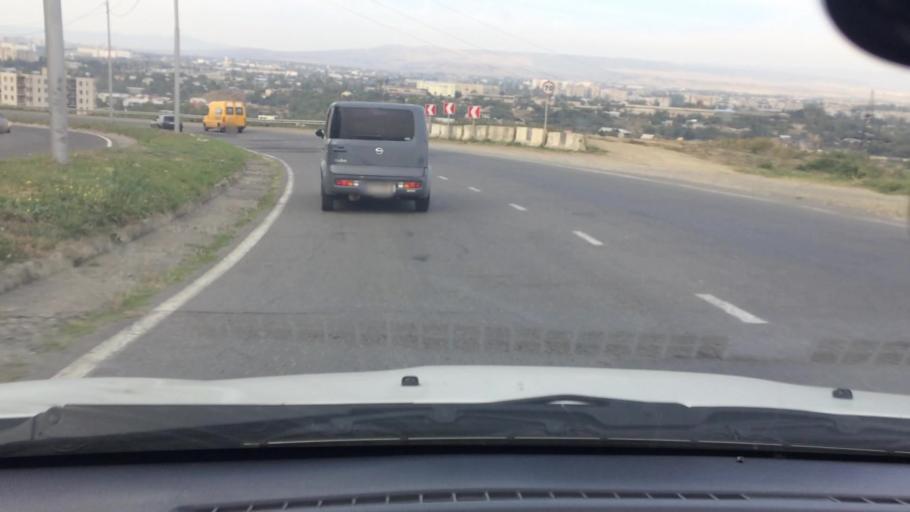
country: GE
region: T'bilisi
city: Tbilisi
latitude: 41.6507
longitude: 44.9051
